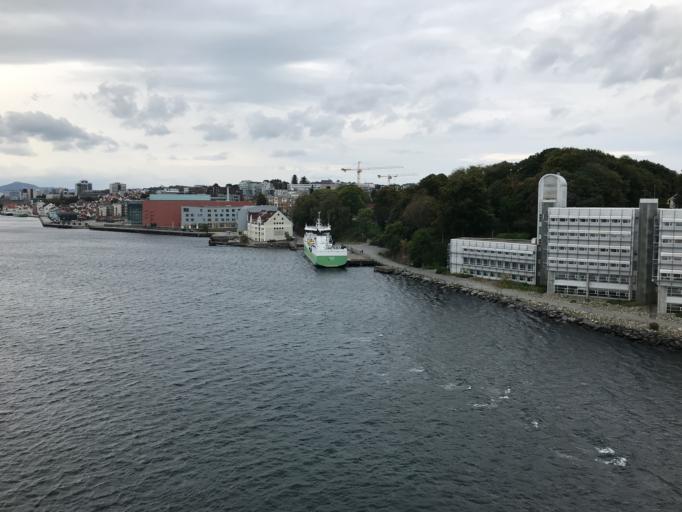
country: NO
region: Rogaland
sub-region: Stavanger
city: Stavanger
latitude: 58.9801
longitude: 5.7220
